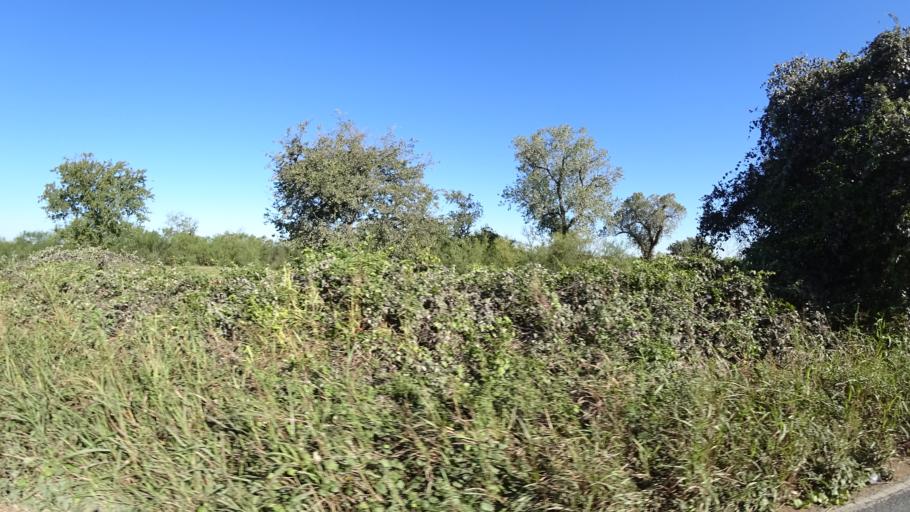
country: US
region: Texas
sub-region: Travis County
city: Austin
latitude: 30.2463
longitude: -97.6746
